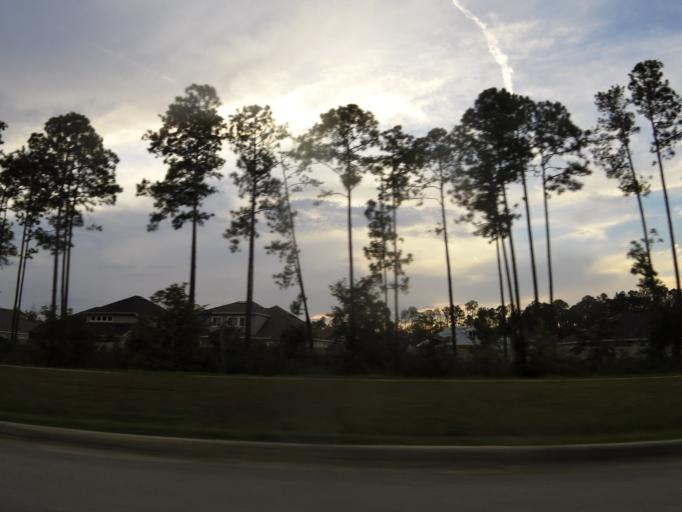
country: US
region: Florida
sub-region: Saint Johns County
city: Fruit Cove
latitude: 30.0620
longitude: -81.6069
